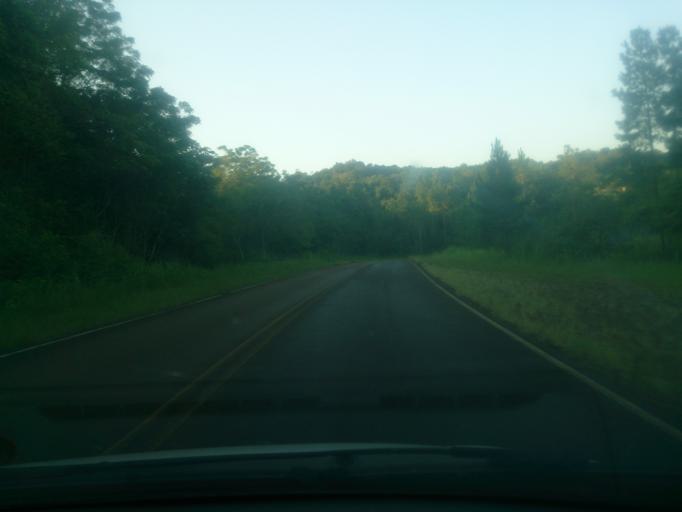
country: AR
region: Misiones
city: Panambi
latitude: -27.6660
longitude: -54.9149
